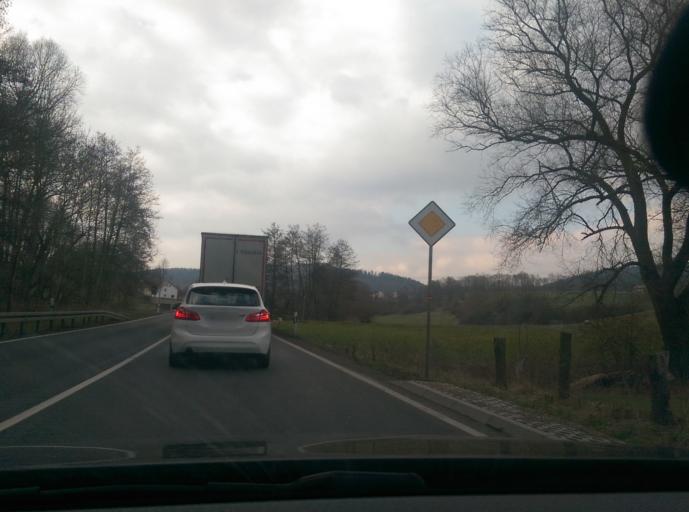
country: DE
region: Thuringia
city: Lauchroden
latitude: 51.0192
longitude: 10.1164
